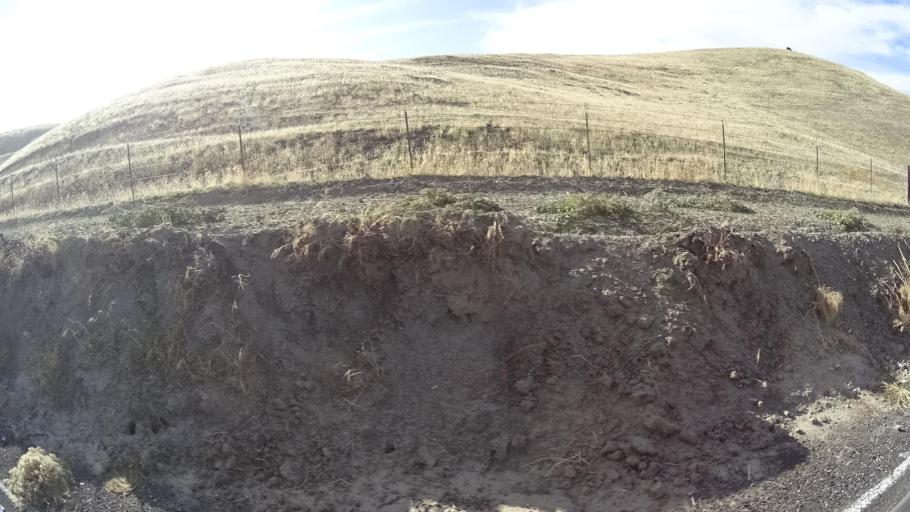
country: US
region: California
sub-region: Kern County
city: Oildale
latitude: 35.6092
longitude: -118.9067
